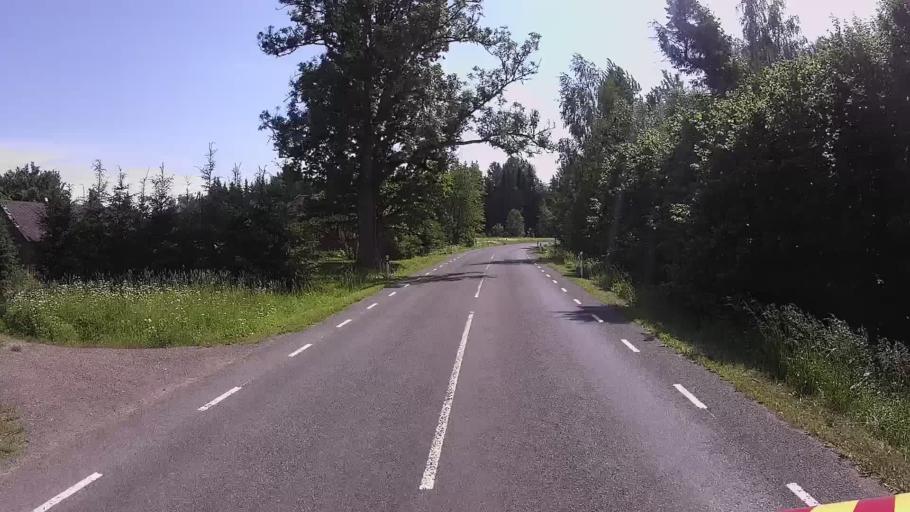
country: EE
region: Viljandimaa
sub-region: Karksi vald
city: Karksi-Nuia
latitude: 58.0394
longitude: 25.5468
